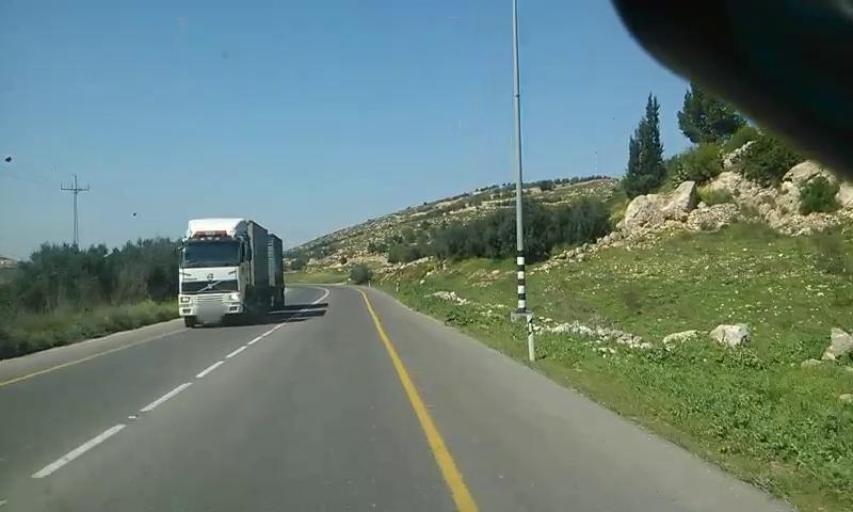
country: PS
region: West Bank
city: Idhna
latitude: 31.5778
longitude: 34.9794
